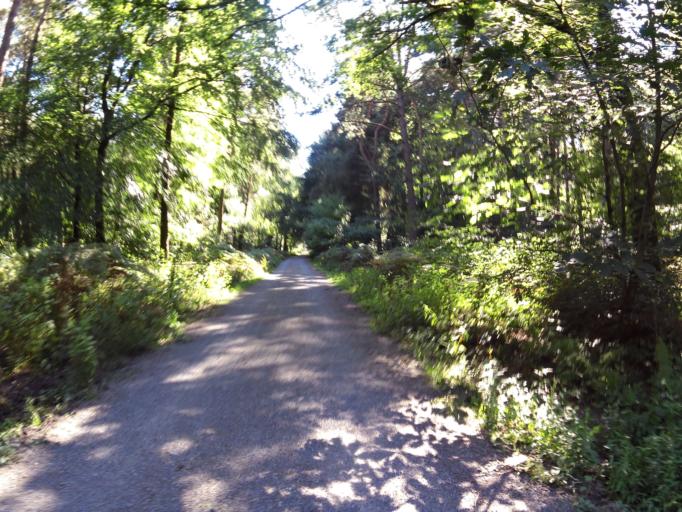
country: NL
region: Gelderland
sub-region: Gemeente Groesbeek
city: De Horst
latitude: 51.7429
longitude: 5.9837
